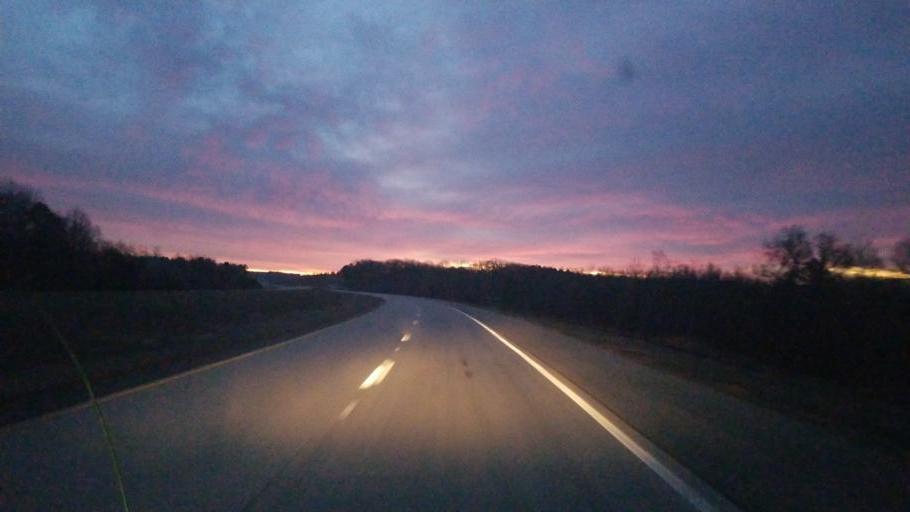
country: US
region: Missouri
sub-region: Shannon County
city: Winona
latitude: 36.9967
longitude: -91.4556
